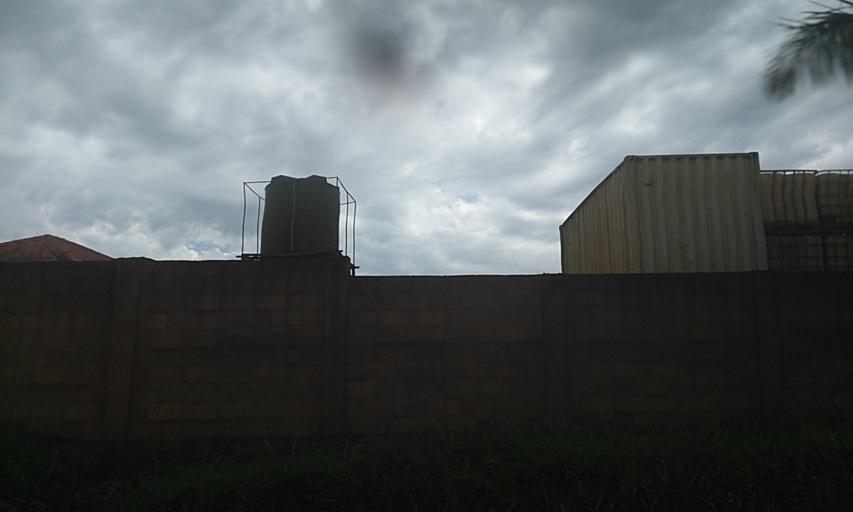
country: UG
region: Central Region
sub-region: Wakiso District
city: Kireka
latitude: 0.4081
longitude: 32.6297
